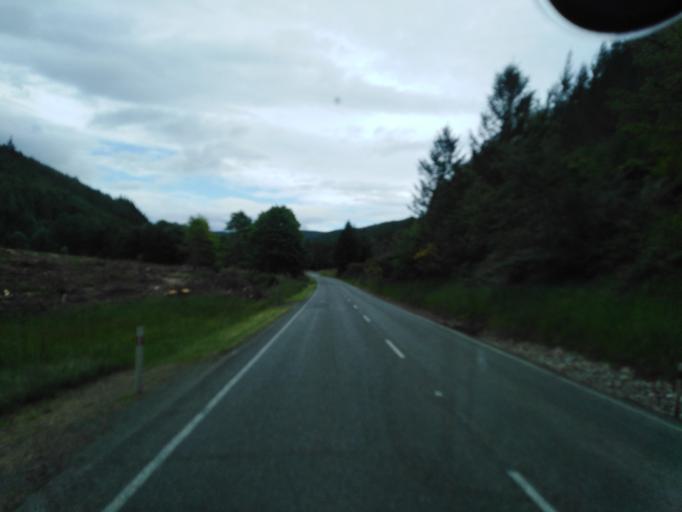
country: NZ
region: Tasman
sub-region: Tasman District
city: Wakefield
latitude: -41.4859
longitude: 172.8887
